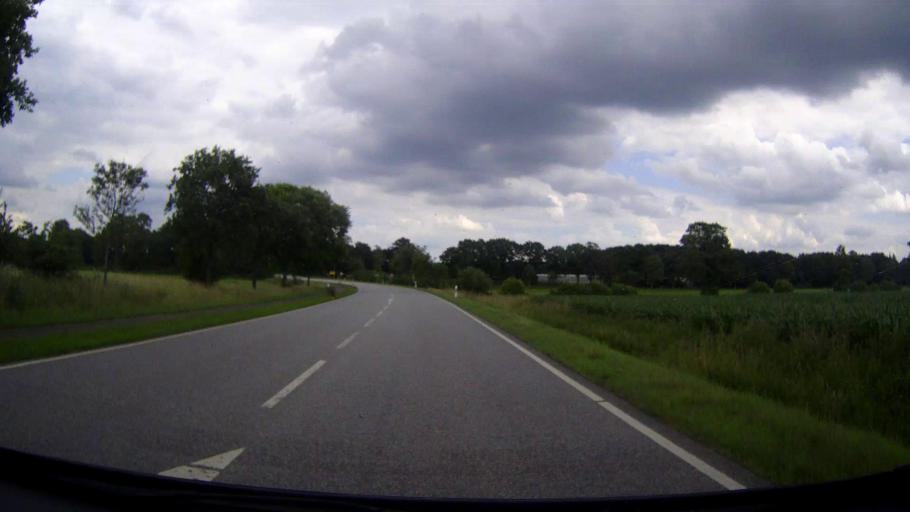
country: DE
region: Schleswig-Holstein
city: Christinenthal
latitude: 54.0523
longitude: 9.5276
